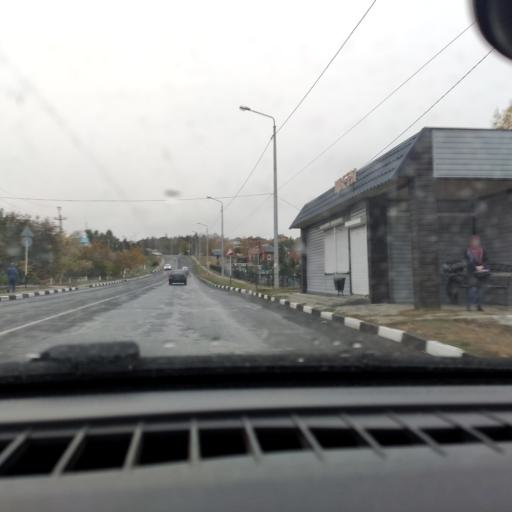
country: RU
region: Belgorod
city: Alekseyevka
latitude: 50.6413
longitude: 38.6928
